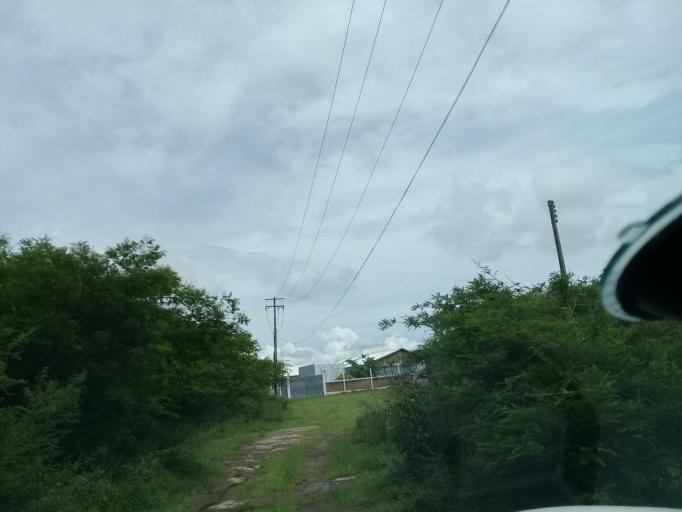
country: MX
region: Veracruz
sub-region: Emiliano Zapata
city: Dos Rios
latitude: 19.4703
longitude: -96.7770
